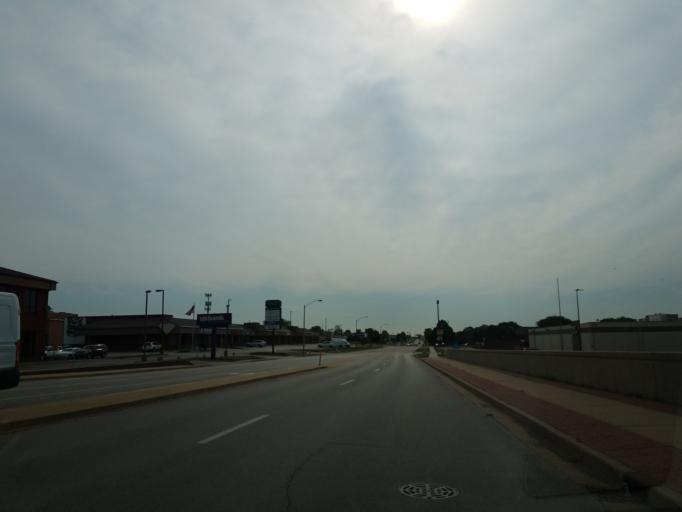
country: US
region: Illinois
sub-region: McLean County
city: Bloomington
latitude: 40.4840
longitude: -88.9522
